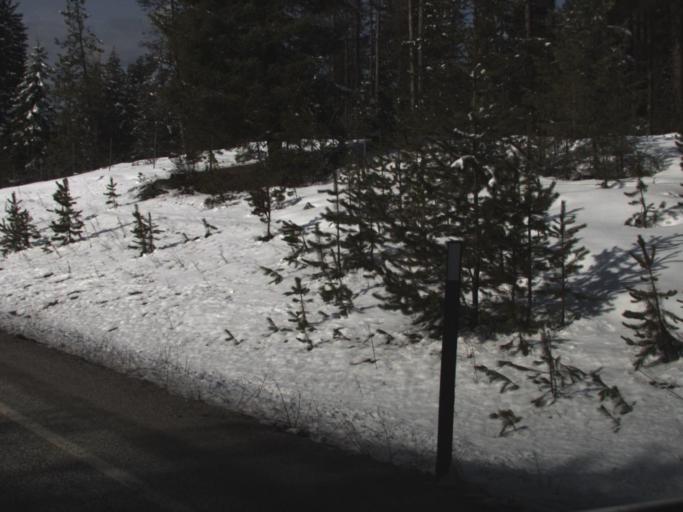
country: US
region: Washington
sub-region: Stevens County
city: Colville
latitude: 48.6702
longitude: -117.4723
